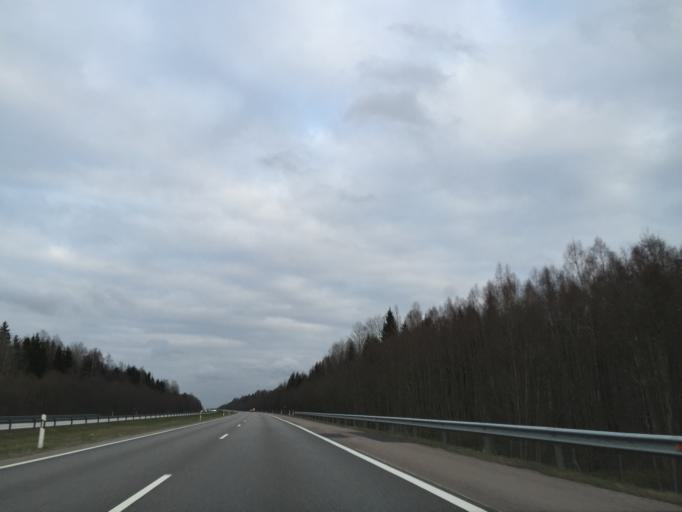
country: LT
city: Rietavas
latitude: 55.6361
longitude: 21.9146
